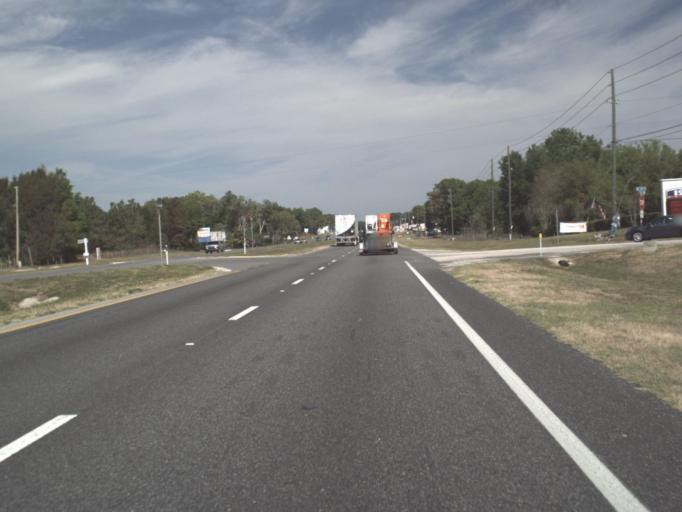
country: US
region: Florida
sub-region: Marion County
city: Belleview
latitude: 29.0381
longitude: -82.0283
